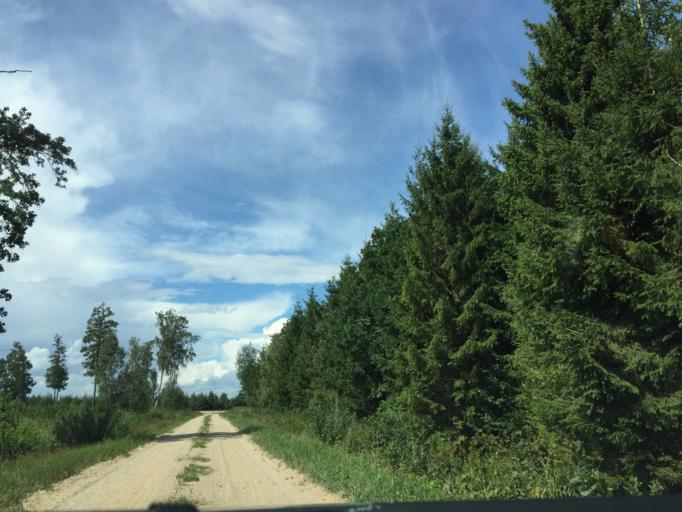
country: LT
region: Siauliu apskritis
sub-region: Joniskis
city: Joniskis
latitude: 56.3025
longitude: 23.6518
